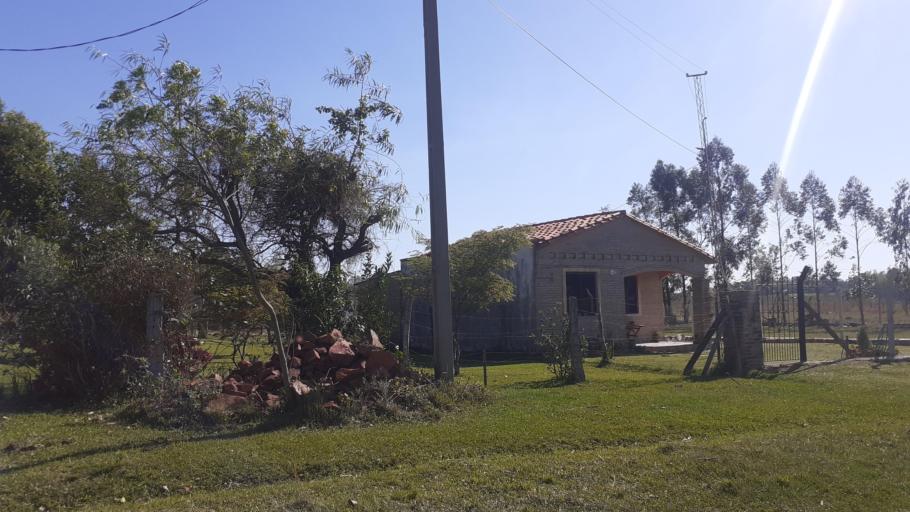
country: PY
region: Misiones
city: San Juan Bautista
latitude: -26.6656
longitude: -57.1235
